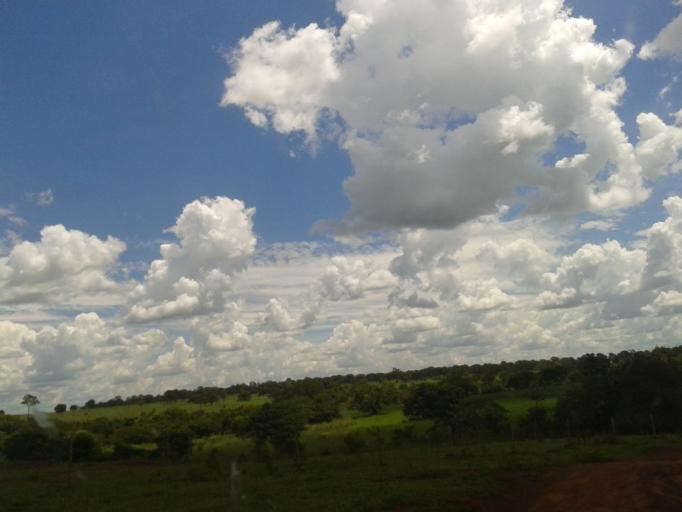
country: BR
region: Minas Gerais
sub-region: Capinopolis
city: Capinopolis
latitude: -18.7854
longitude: -49.8008
